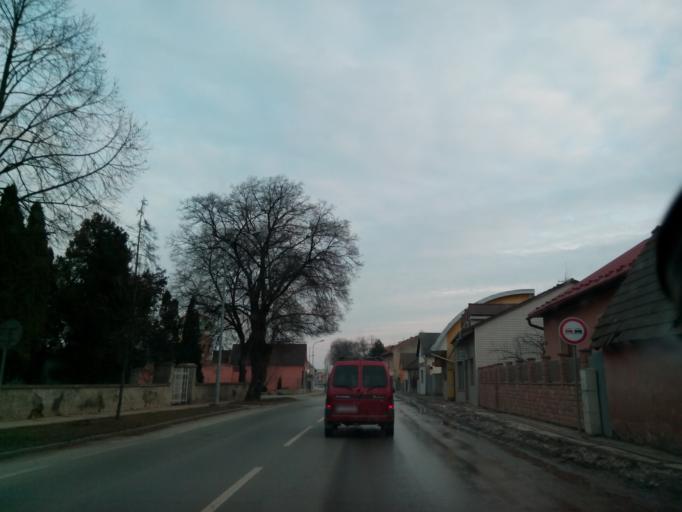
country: SK
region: Presovsky
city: Sabinov
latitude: 49.1055
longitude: 21.0890
